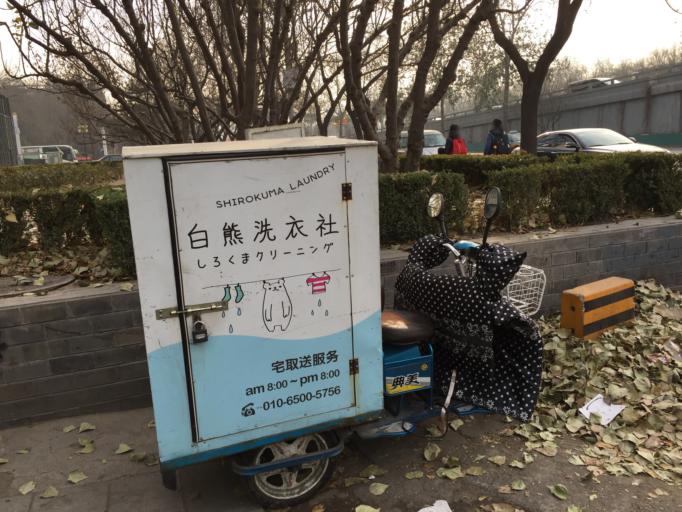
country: CN
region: Beijing
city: Chaowai
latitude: 39.9451
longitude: 116.4562
